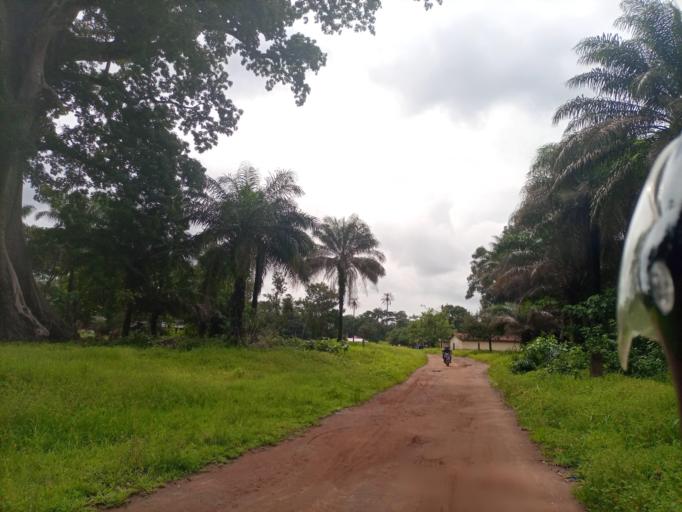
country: SL
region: Northern Province
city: Sawkta
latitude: 8.6363
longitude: -13.1949
